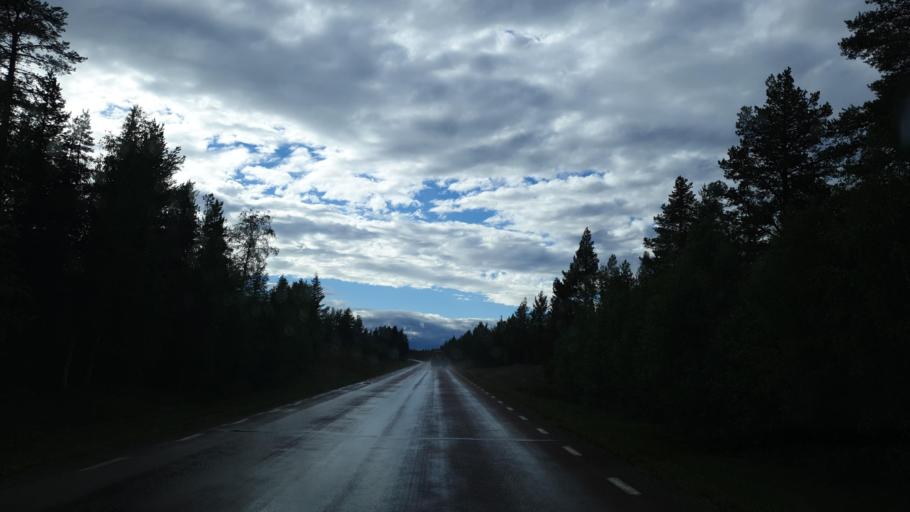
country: SE
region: Norrbotten
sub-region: Arjeplogs Kommun
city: Arjeplog
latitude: 65.9934
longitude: 18.1741
